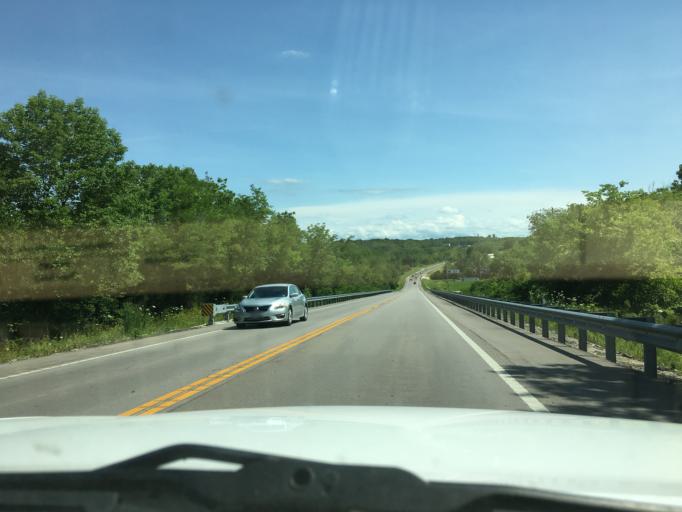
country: US
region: Missouri
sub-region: Franklin County
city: Union
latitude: 38.5031
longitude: -91.0047
